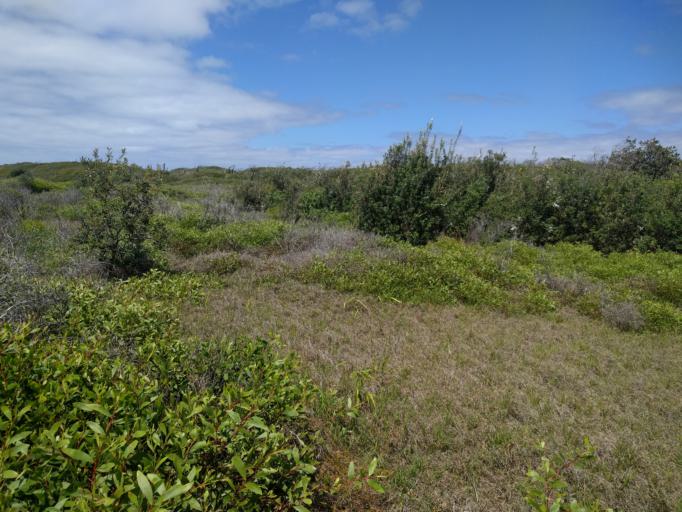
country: AU
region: Queensland
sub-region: Gympie Regional Council
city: Rainbow Beach
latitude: -25.7473
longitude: 153.0865
